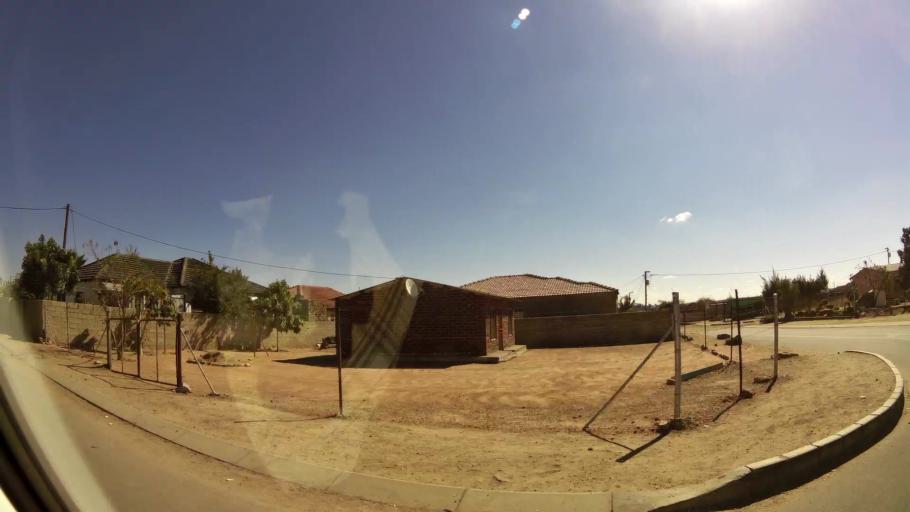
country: ZA
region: Limpopo
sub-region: Capricorn District Municipality
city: Polokwane
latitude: -23.8491
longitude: 29.4111
